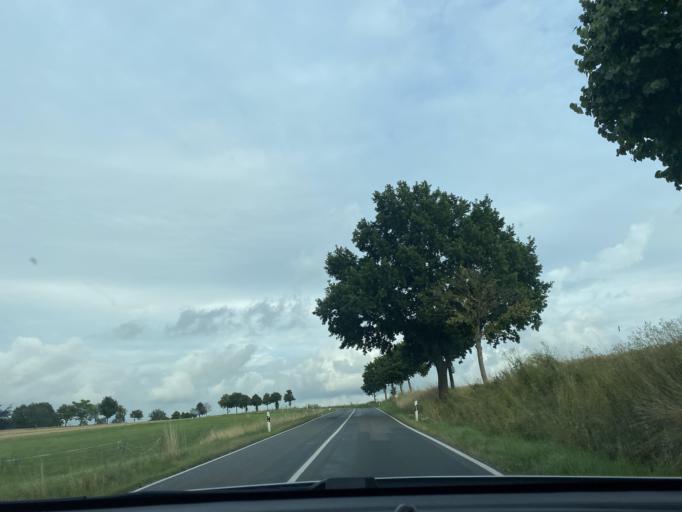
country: DE
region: Saxony
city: Grosshennersdorf
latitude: 51.0193
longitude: 14.7933
